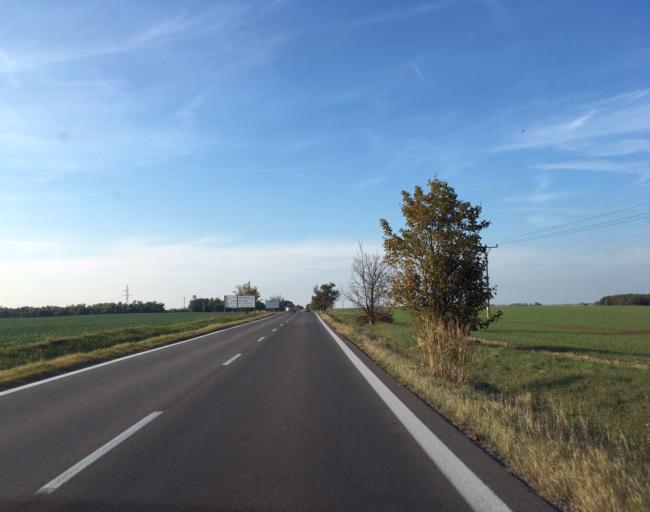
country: SK
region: Nitriansky
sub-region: Okres Nove Zamky
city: Nove Zamky
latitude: 48.0212
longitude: 18.1442
